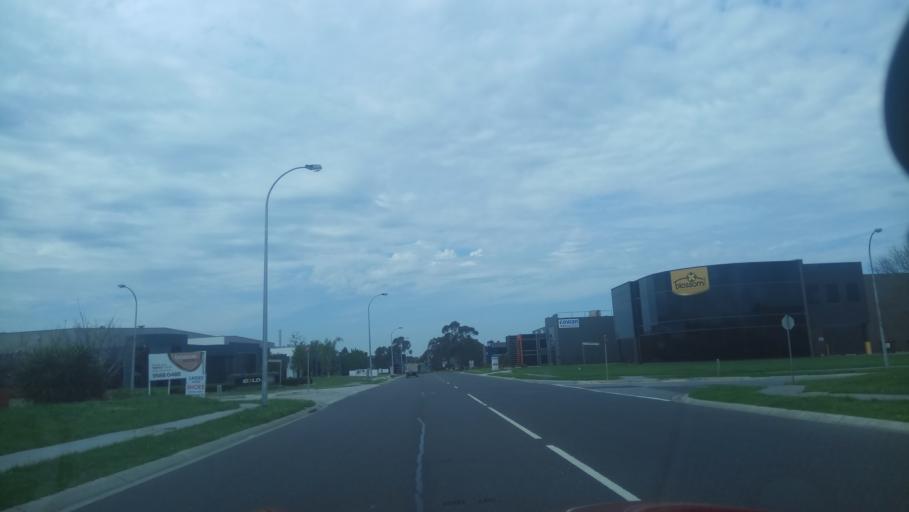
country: AU
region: Victoria
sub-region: Kingston
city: Waterways
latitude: -38.0013
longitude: 145.1155
